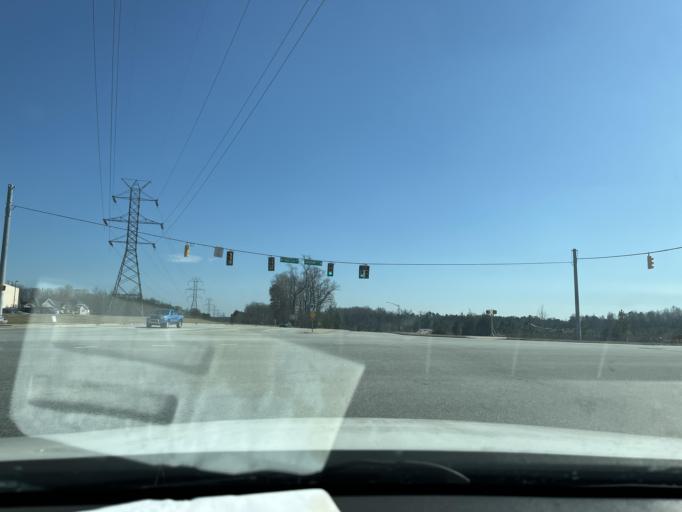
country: US
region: North Carolina
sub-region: Guilford County
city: Jamestown
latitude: 36.0004
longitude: -79.9081
